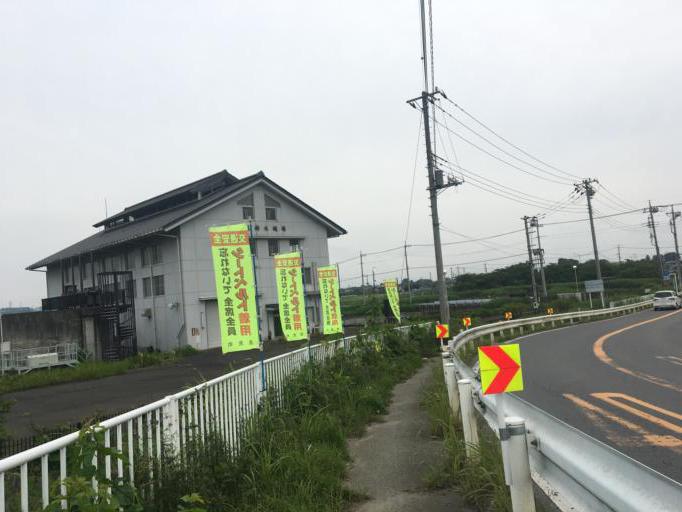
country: JP
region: Saitama
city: Sakado
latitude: 36.0189
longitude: 139.4389
